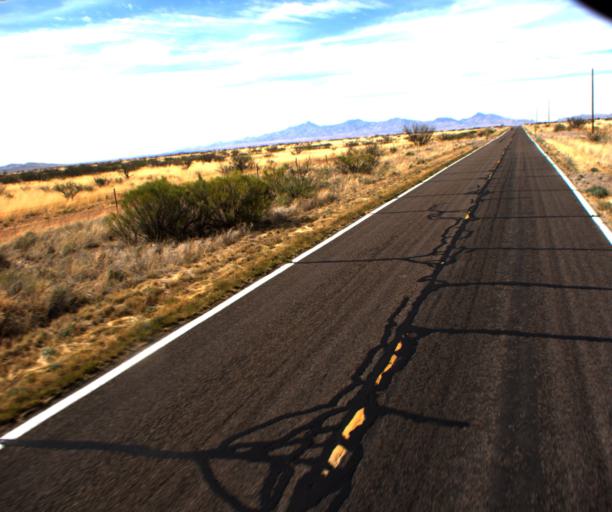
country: US
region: Arizona
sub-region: Cochise County
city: Willcox
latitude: 31.9231
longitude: -109.4914
